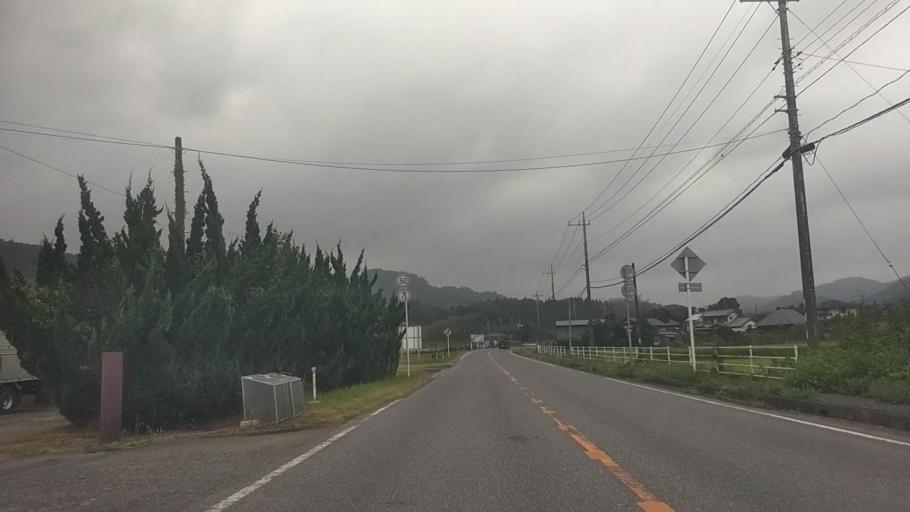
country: JP
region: Chiba
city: Kawaguchi
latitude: 35.1369
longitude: 139.9830
